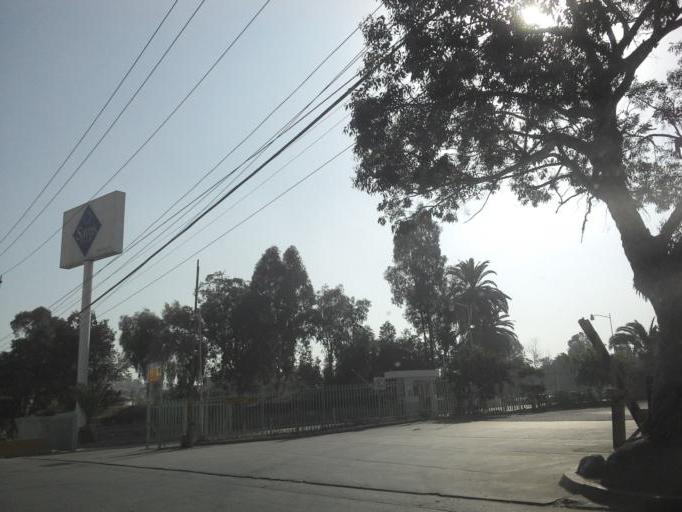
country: MX
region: Baja California
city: Tijuana
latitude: 32.5169
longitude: -117.0055
